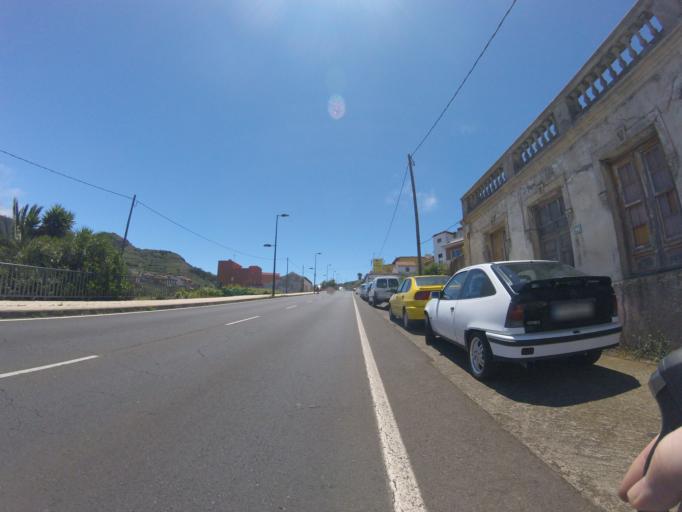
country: ES
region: Canary Islands
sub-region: Provincia de Santa Cruz de Tenerife
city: Tegueste
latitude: 28.5160
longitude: -16.3183
